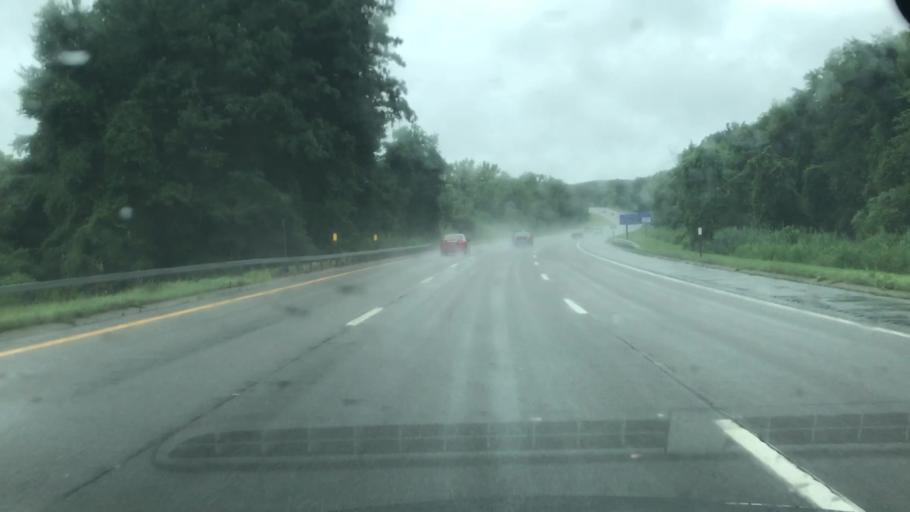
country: US
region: New York
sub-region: Westchester County
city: Briarcliff Manor
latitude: 41.2073
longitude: -73.8093
